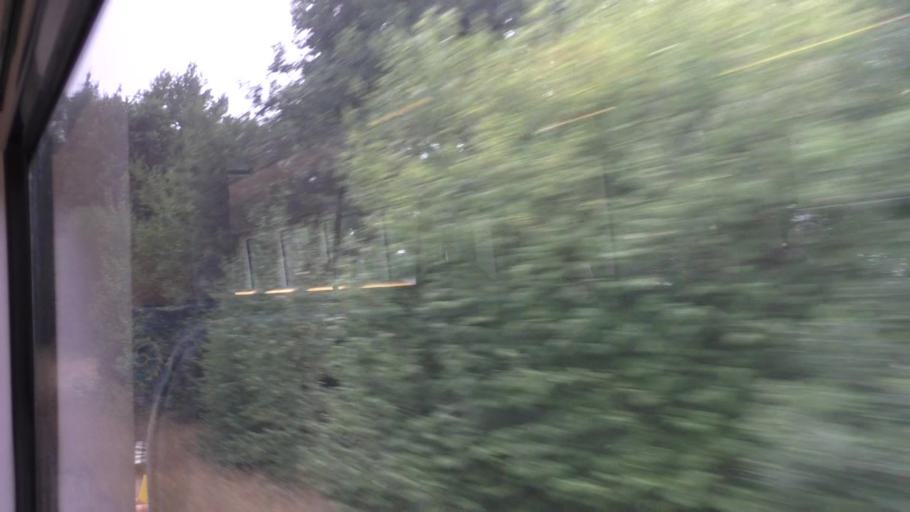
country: DE
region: Saxony
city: Goerlitz
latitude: 51.1673
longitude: 14.9631
